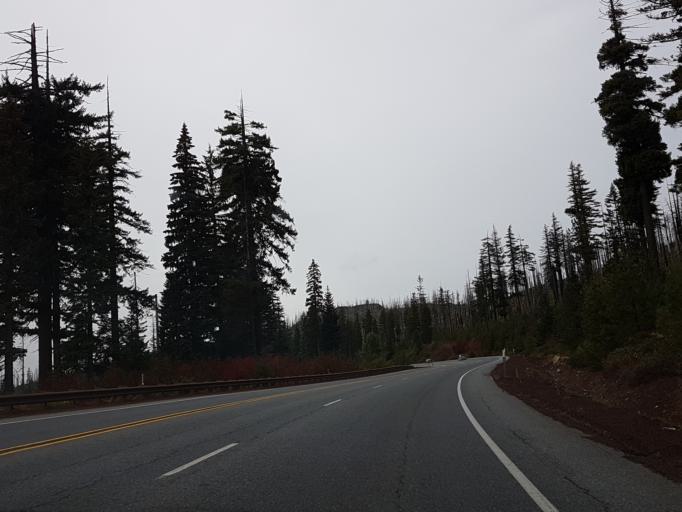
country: US
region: Oregon
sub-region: Deschutes County
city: Sisters
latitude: 44.4212
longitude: -121.7906
